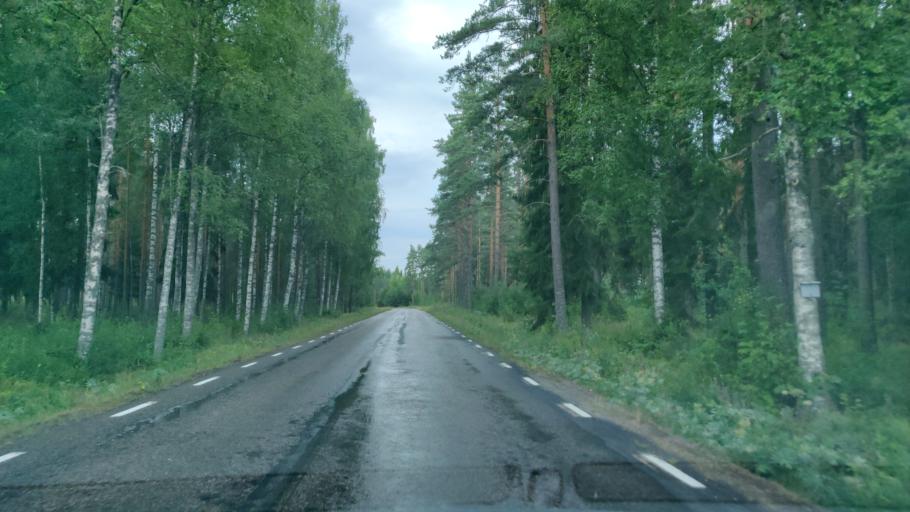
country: SE
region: Vaermland
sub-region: Munkfors Kommun
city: Munkfors
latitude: 59.8832
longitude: 13.5223
